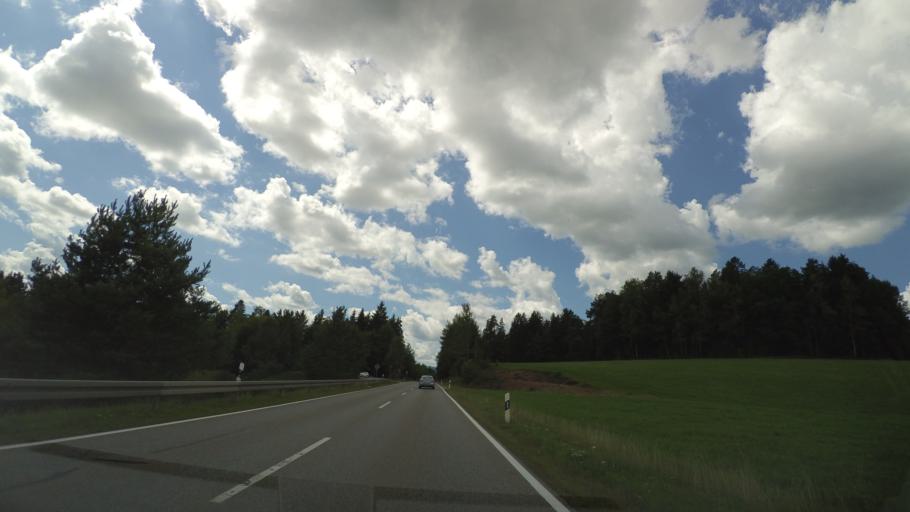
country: DE
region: Bavaria
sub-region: Lower Bavaria
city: Bobrach
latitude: 49.0496
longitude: 13.0287
